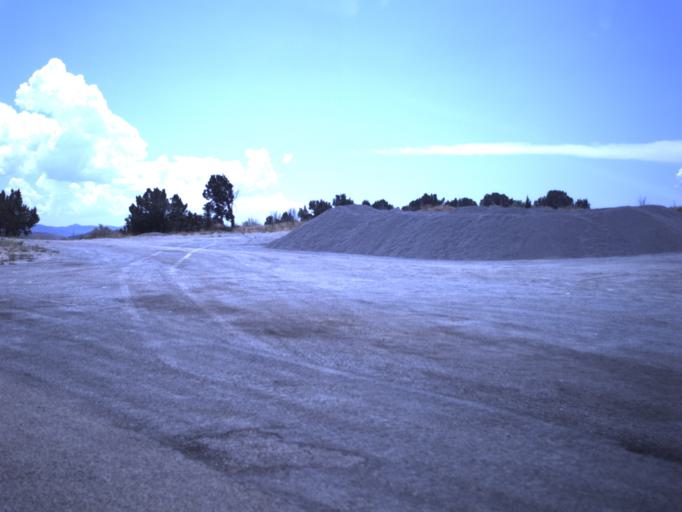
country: US
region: Utah
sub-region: Juab County
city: Nephi
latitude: 39.6669
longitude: -112.0501
